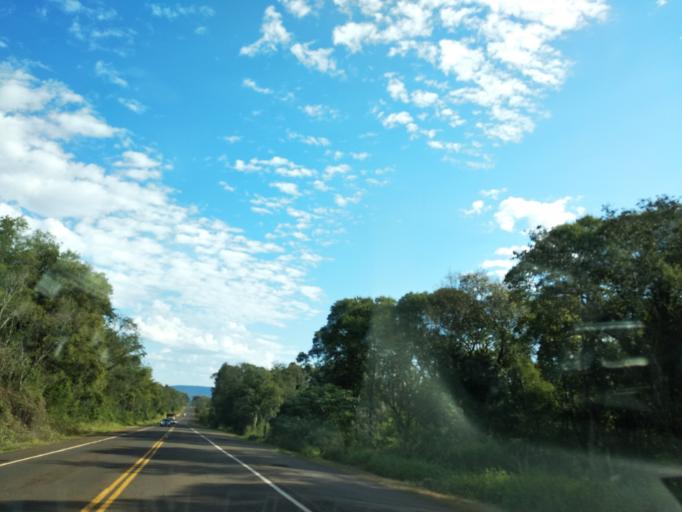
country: AR
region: Misiones
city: Aristobulo del Valle
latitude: -27.0924
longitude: -54.9504
